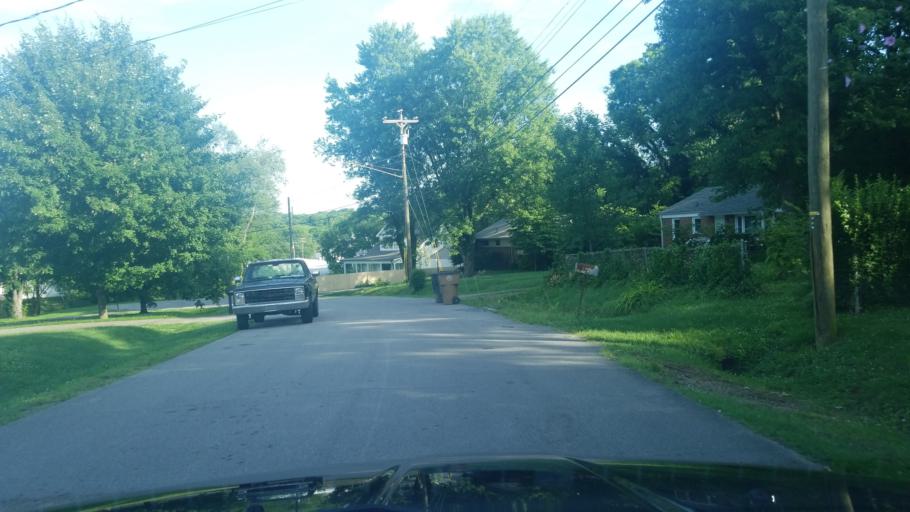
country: US
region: Tennessee
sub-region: Davidson County
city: Oak Hill
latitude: 36.1133
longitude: -86.7386
